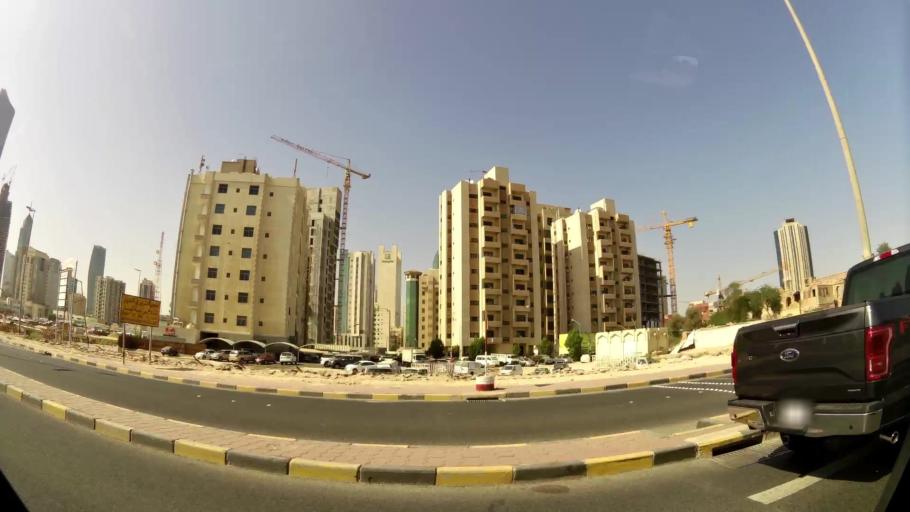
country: KW
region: Al Asimah
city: Ad Dasmah
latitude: 29.3876
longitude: 47.9952
